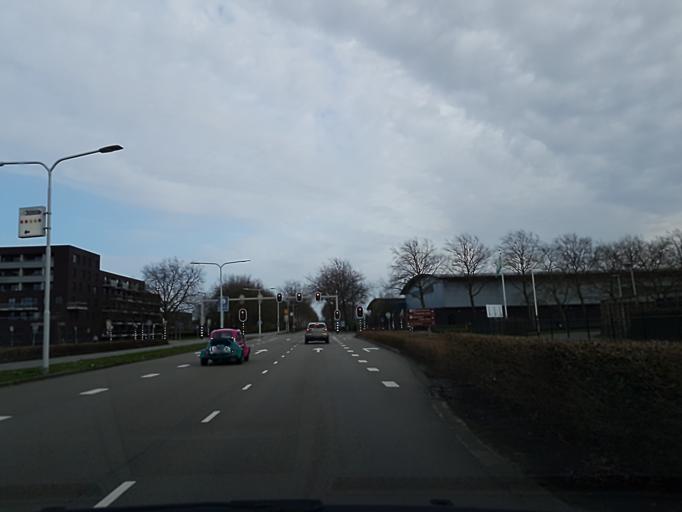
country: NL
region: Zeeland
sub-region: Gemeente Terneuzen
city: Terneuzen
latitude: 51.3195
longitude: 3.8435
